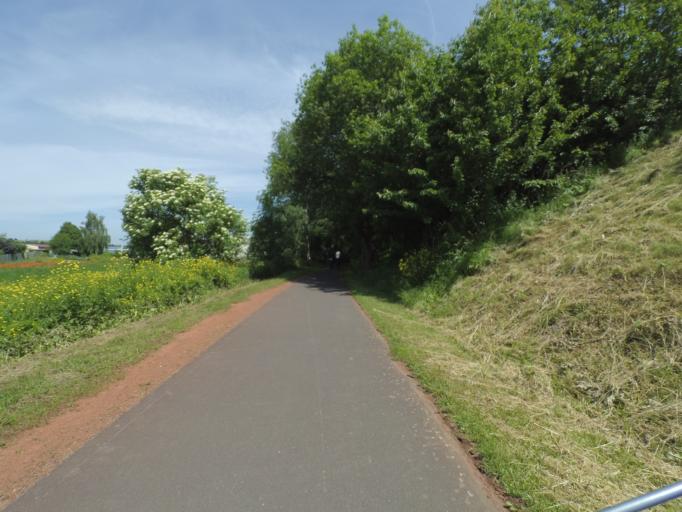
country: DE
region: Rheinland-Pfalz
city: Polch
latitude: 50.3079
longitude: 7.3189
